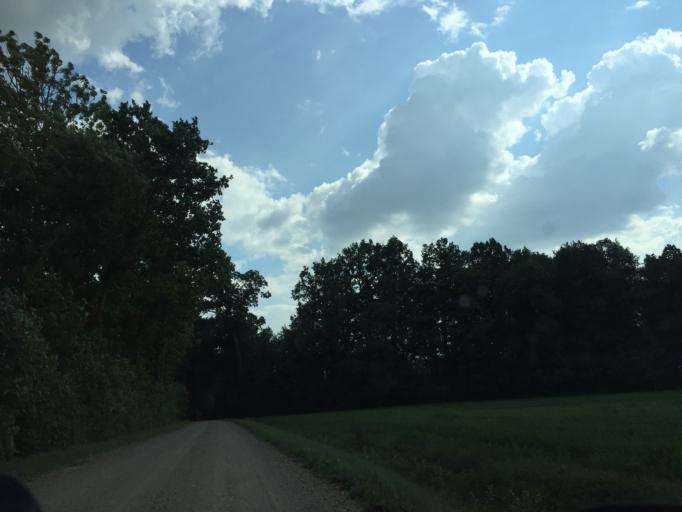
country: LV
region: Jelgava
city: Jelgava
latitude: 56.5070
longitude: 23.7549
